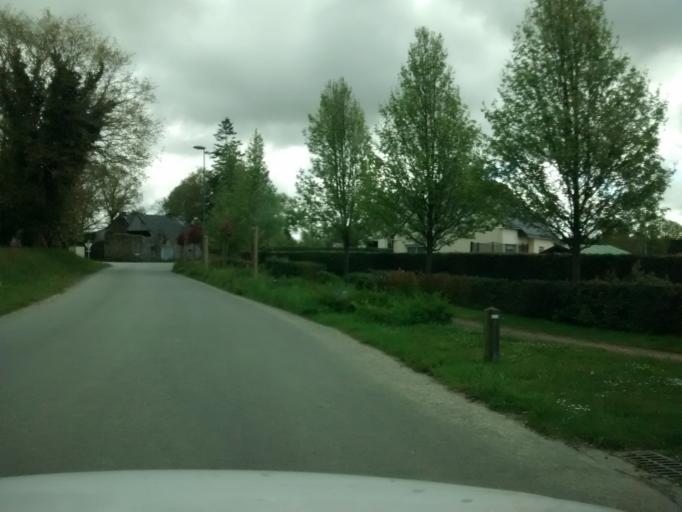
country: FR
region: Brittany
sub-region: Departement du Morbihan
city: Ruffiac
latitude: 47.8022
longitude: -2.2266
